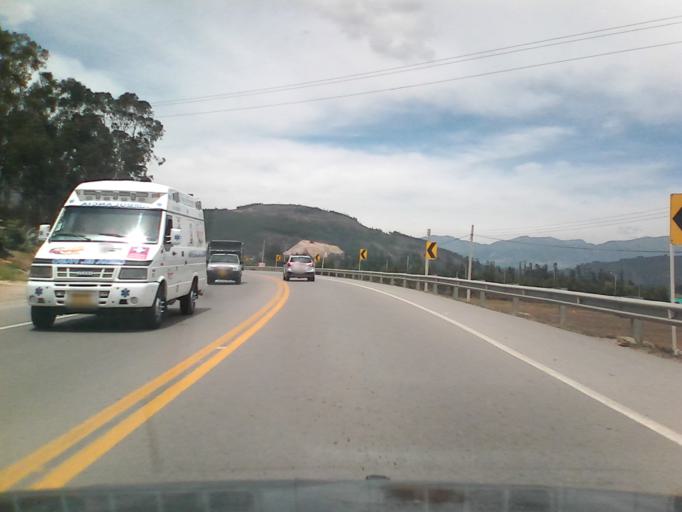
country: CO
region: Boyaca
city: Tibasosa
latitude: 5.7432
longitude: -72.9786
